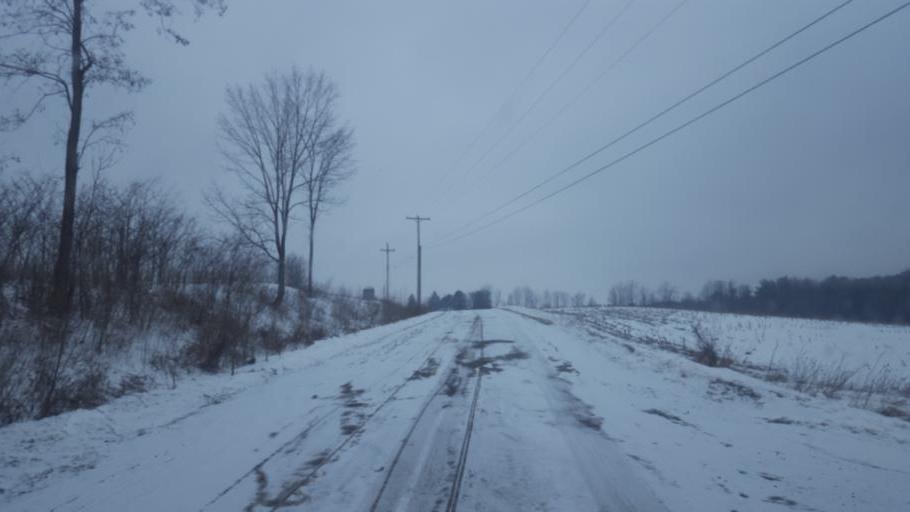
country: US
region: Pennsylvania
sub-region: Tioga County
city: Elkland
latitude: 42.1029
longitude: -77.4642
